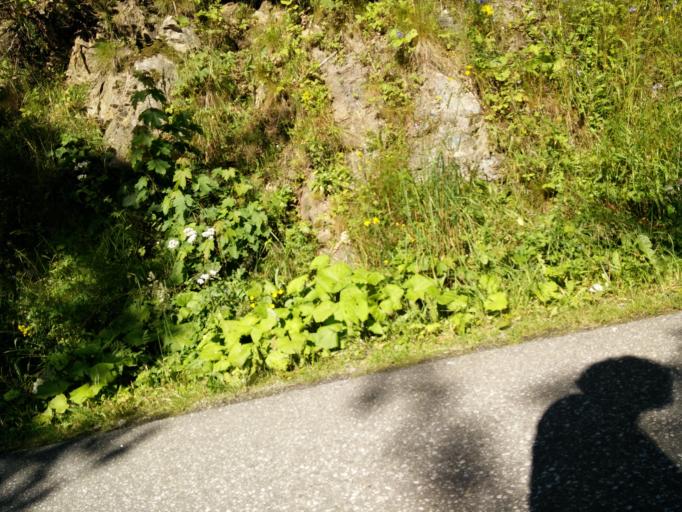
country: NO
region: More og Romsdal
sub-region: Kristiansund
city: Rensvik
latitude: 63.0215
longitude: 7.9478
